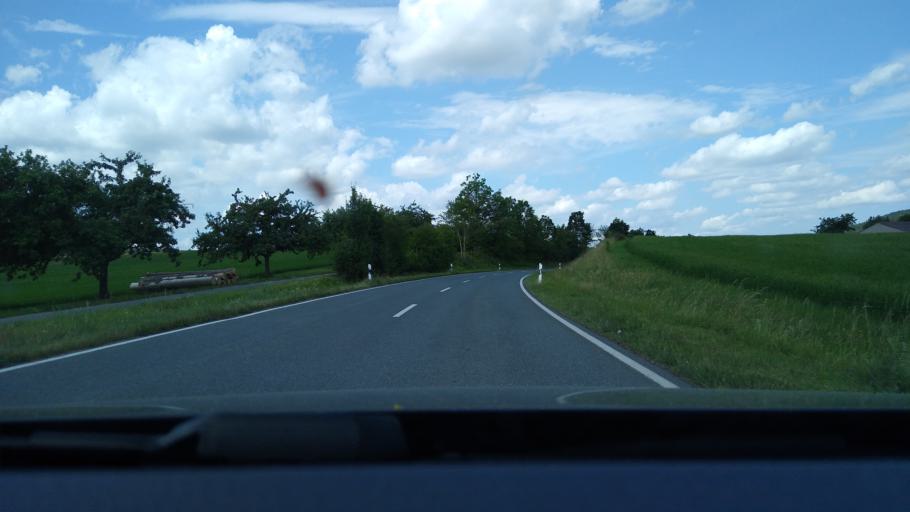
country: DE
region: Bavaria
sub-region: Regierungsbezirk Mittelfranken
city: Trautskirchen
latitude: 49.4570
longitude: 10.5779
